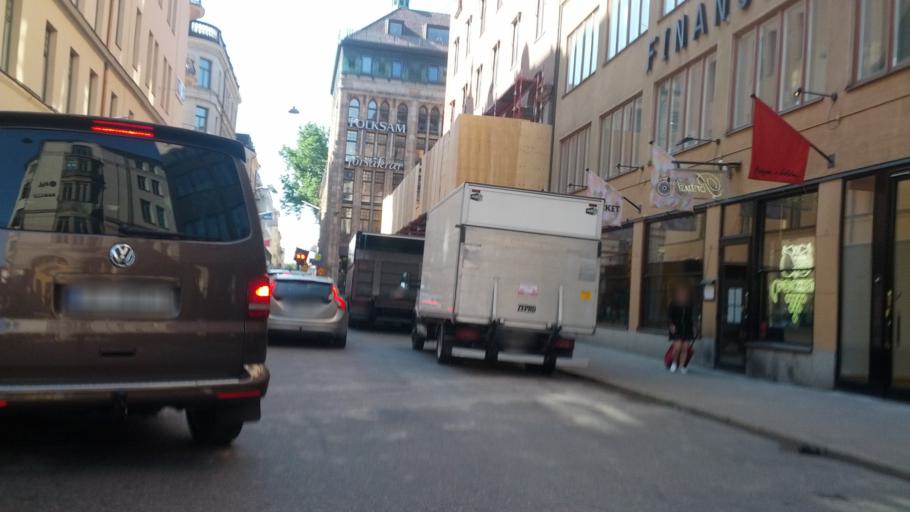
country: SE
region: Stockholm
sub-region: Stockholms Kommun
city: Stockholm
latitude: 59.3369
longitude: 18.0711
